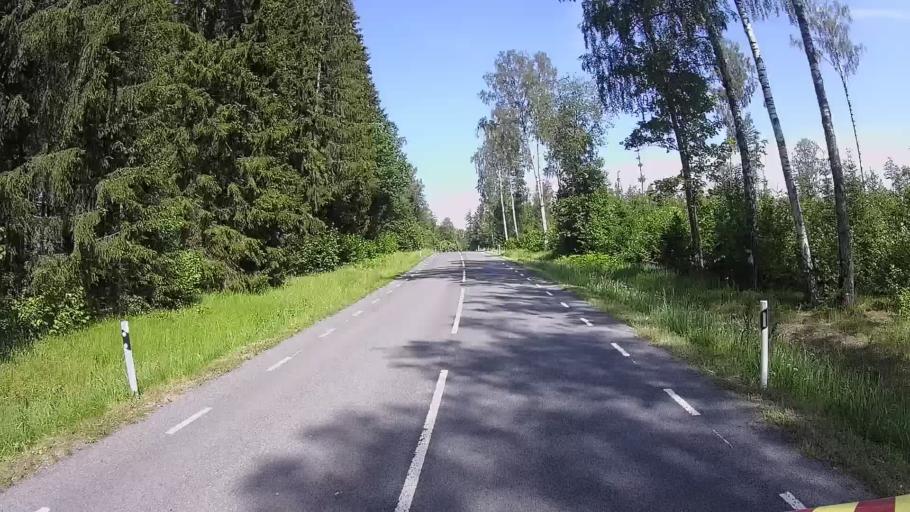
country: LV
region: Naukseni
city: Naukseni
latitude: 57.9896
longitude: 25.5023
